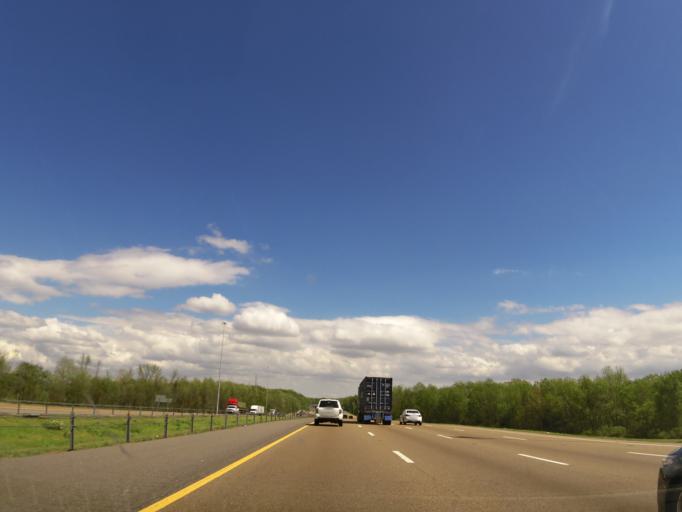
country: US
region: Tennessee
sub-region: Shelby County
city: Bartlett
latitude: 35.1904
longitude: -89.9558
